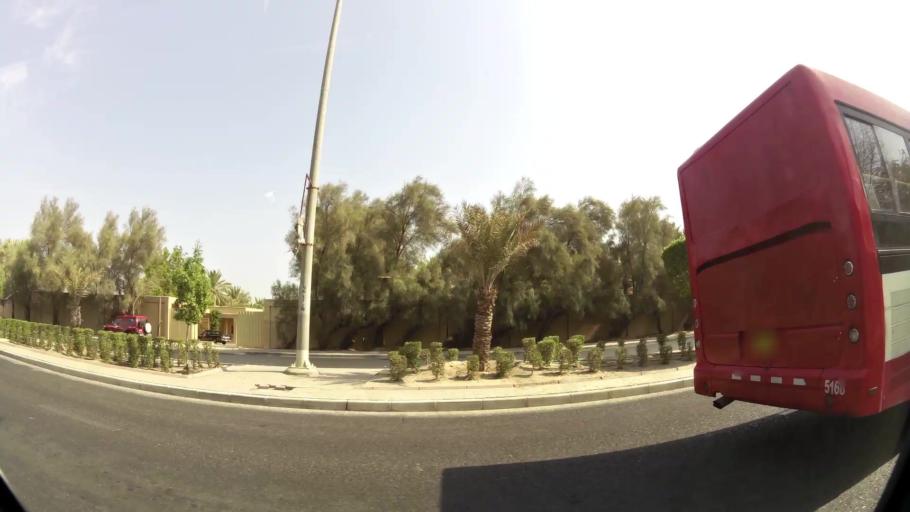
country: KW
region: Al Ahmadi
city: Al Fintas
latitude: 29.1606
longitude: 48.1219
